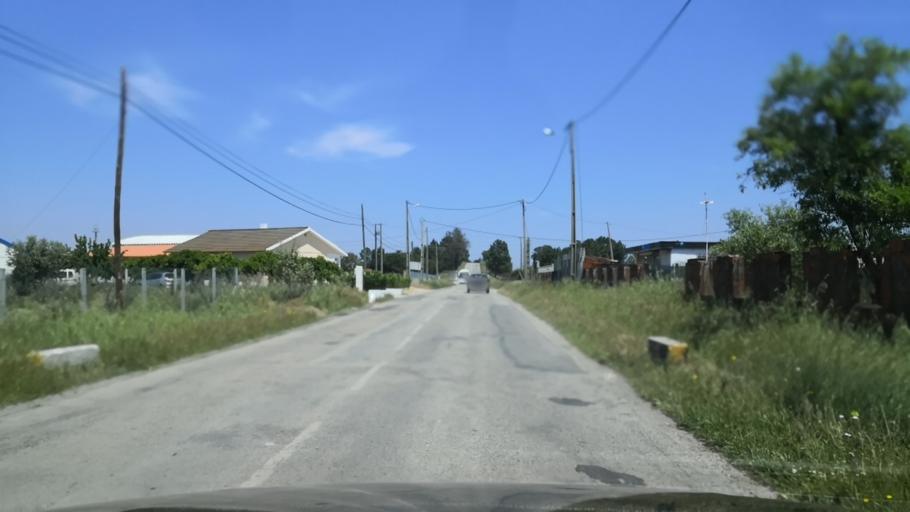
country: PT
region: Setubal
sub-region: Palmela
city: Palmela
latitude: 38.6176
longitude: -8.7529
